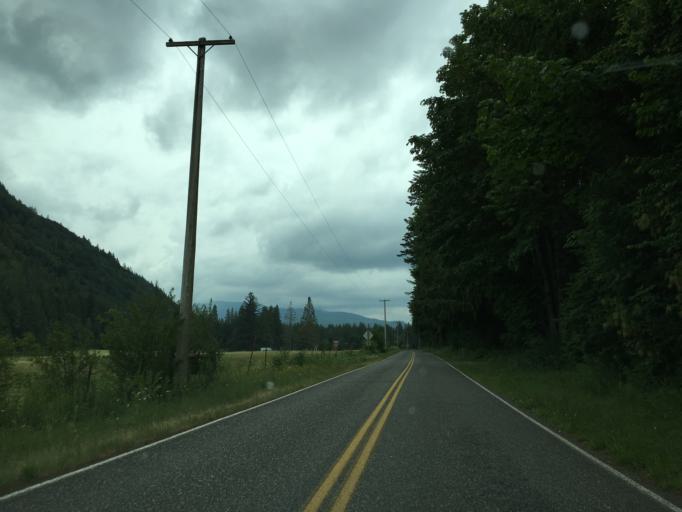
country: US
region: Washington
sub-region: Whatcom County
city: Peaceful Valley
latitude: 48.9924
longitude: -122.0947
